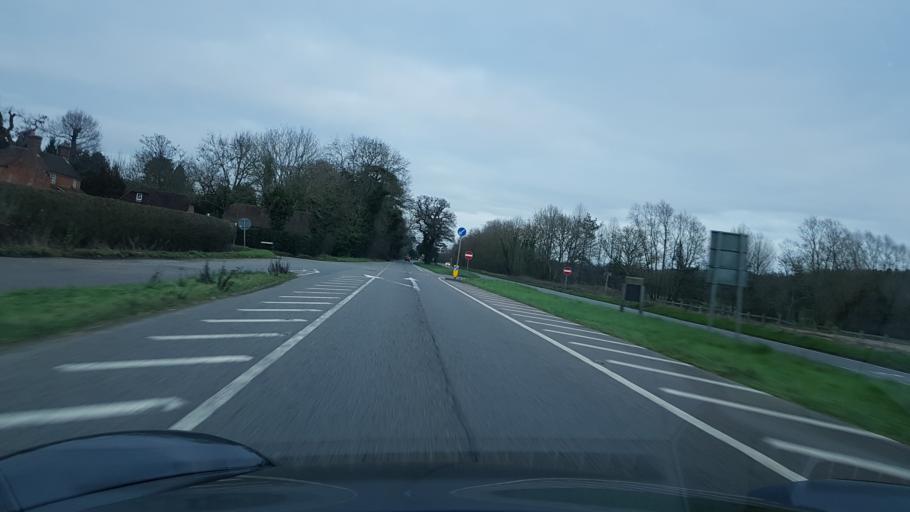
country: GB
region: England
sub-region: Surrey
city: Farnham
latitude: 51.1937
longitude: -0.8485
